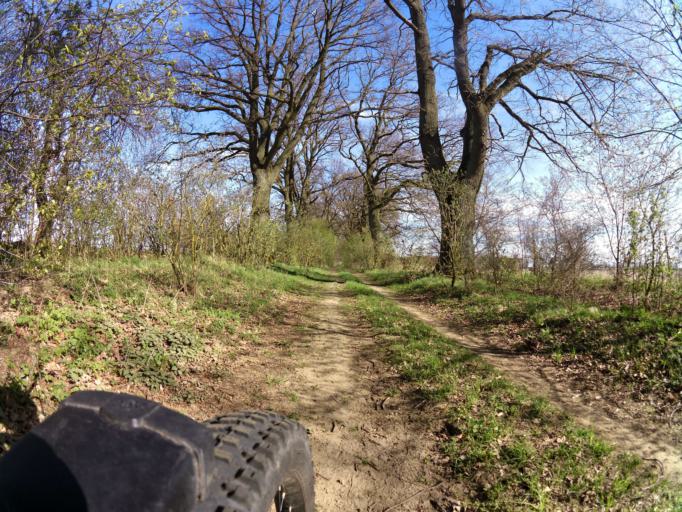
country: PL
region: West Pomeranian Voivodeship
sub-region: Powiat lobeski
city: Resko
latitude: 53.7815
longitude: 15.5514
